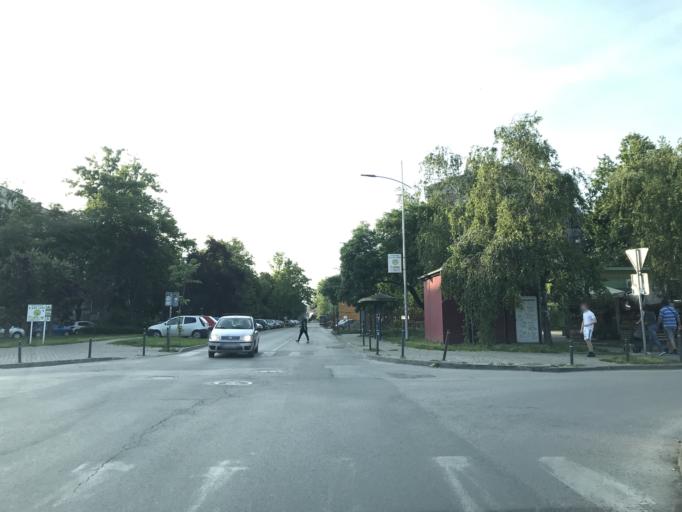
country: RS
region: Autonomna Pokrajina Vojvodina
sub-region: Juznobacki Okrug
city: Novi Sad
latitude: 45.2636
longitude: 19.8115
